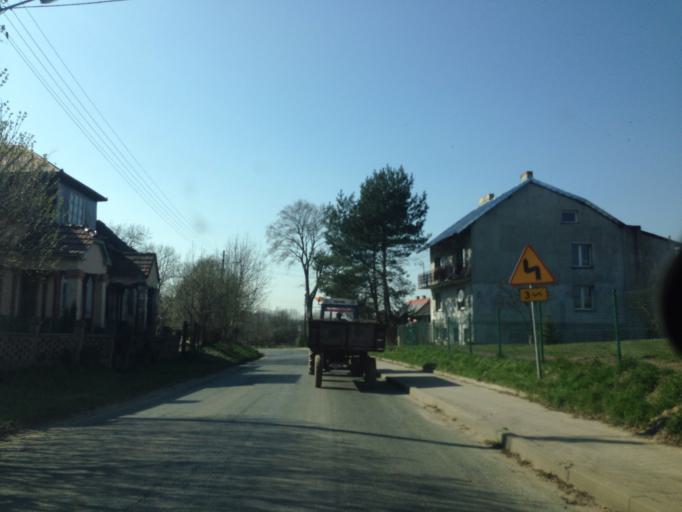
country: PL
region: Lower Silesian Voivodeship
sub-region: Powiat olesnicki
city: Bierutow
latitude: 51.1937
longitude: 17.4984
